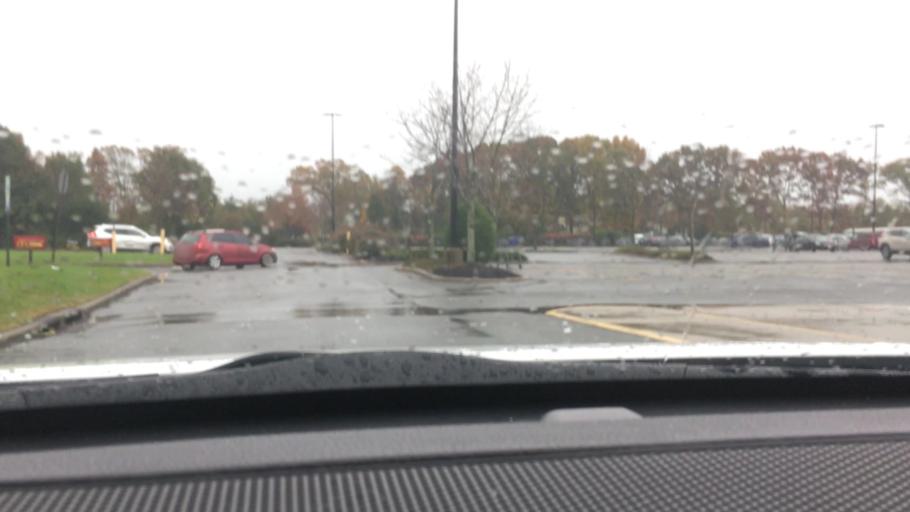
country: US
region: New Jersey
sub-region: Atlantic County
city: Pleasantville
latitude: 39.3944
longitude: -74.5434
